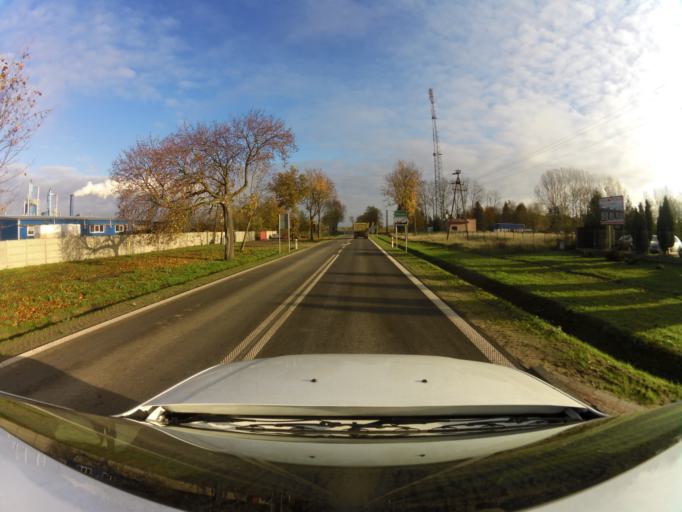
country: PL
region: West Pomeranian Voivodeship
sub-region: Powiat gryficki
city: Gryfice
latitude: 53.9286
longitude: 15.2080
